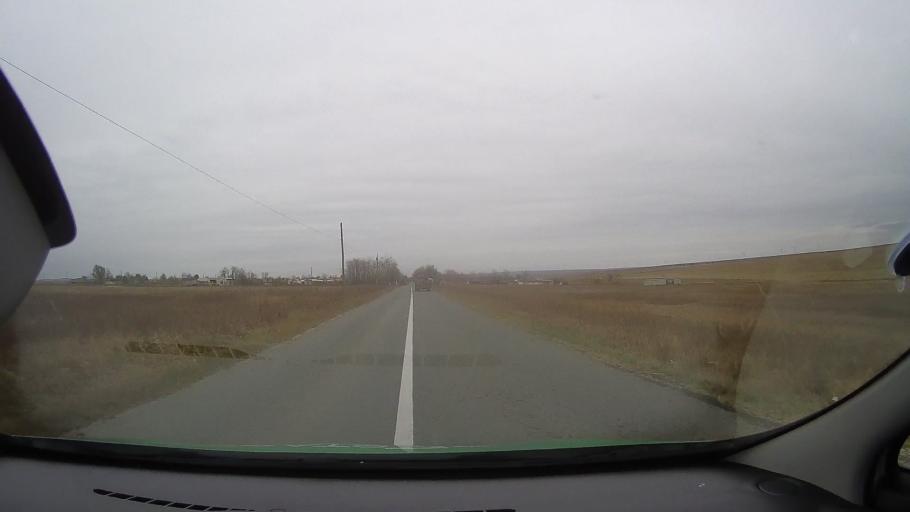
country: RO
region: Constanta
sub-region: Comuna Silistea
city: Silistea
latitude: 44.4393
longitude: 28.2290
